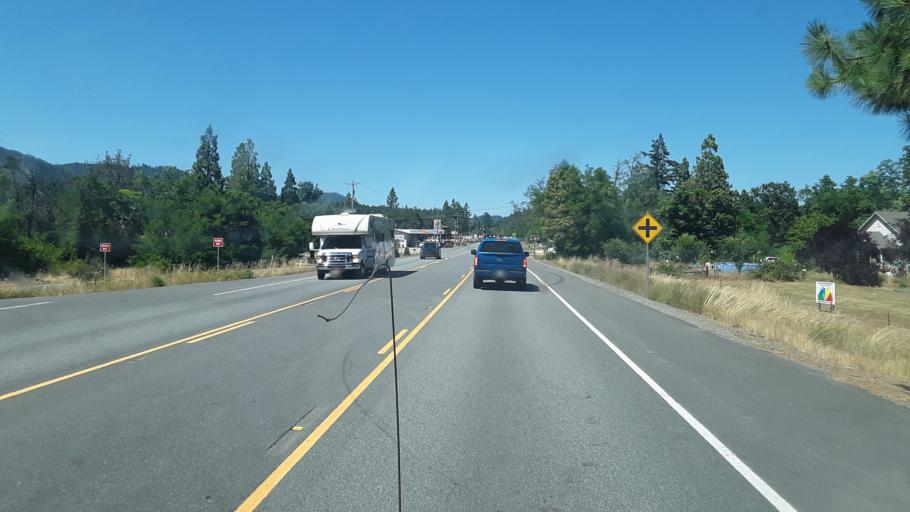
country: US
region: Oregon
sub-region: Josephine County
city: Cave Junction
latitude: 42.2769
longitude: -123.6168
